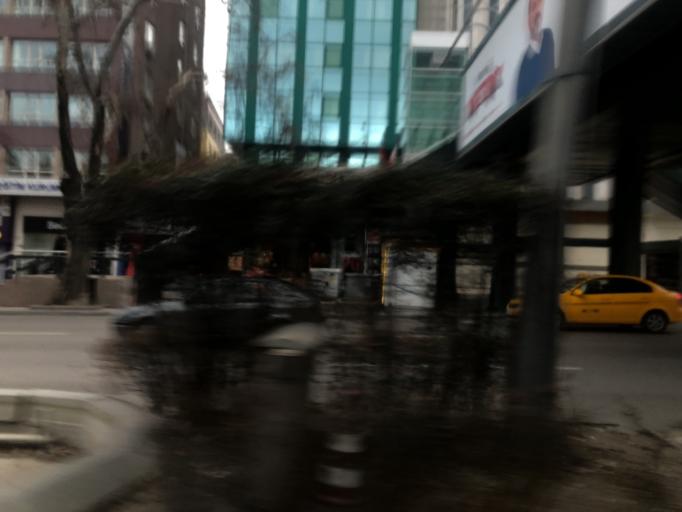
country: TR
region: Ankara
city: Ankara
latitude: 39.9162
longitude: 32.8541
